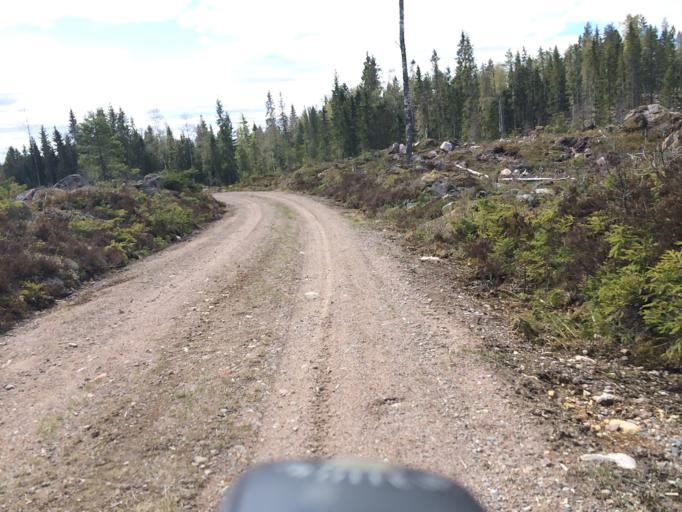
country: SE
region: OErebro
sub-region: Hallefors Kommun
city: Haellefors
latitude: 60.0504
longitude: 14.5155
